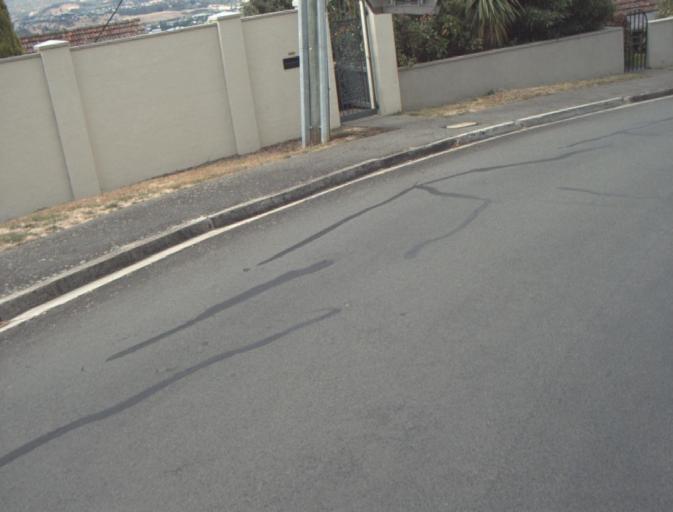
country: AU
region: Tasmania
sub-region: Launceston
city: Launceston
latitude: -41.4323
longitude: 147.1140
